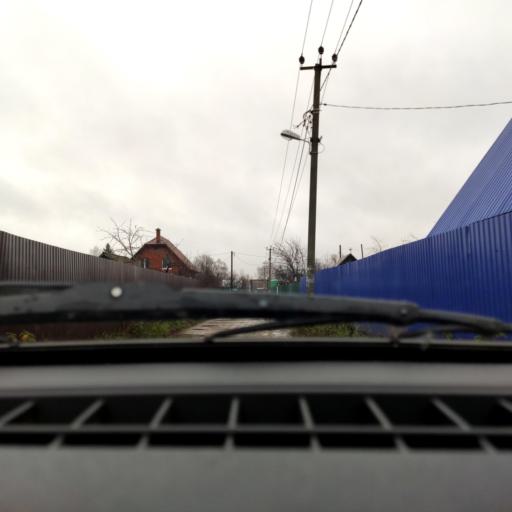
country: RU
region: Bashkortostan
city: Ufa
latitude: 54.8107
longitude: 56.1534
